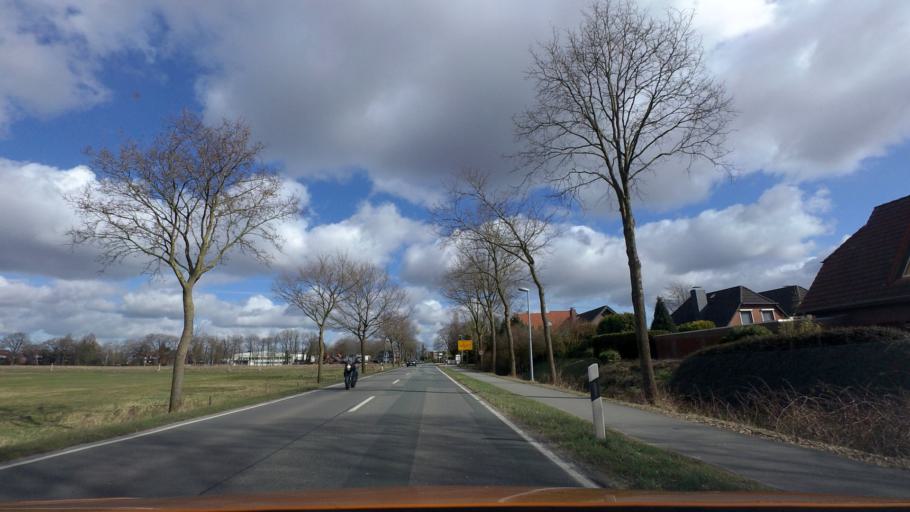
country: DE
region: Lower Saxony
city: Oldenburg
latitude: 53.1400
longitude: 8.1424
